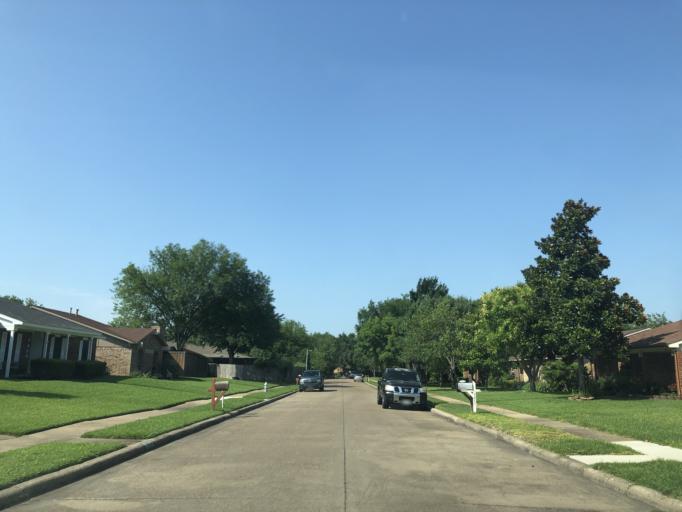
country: US
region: Texas
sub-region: Dallas County
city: Sunnyvale
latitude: 32.8226
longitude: -96.5991
